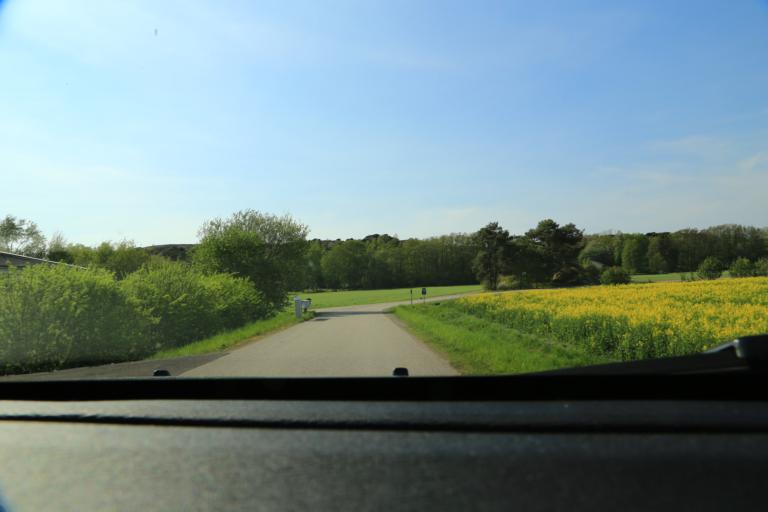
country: SE
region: Halland
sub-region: Varbergs Kommun
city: Varberg
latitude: 57.1568
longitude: 12.2420
